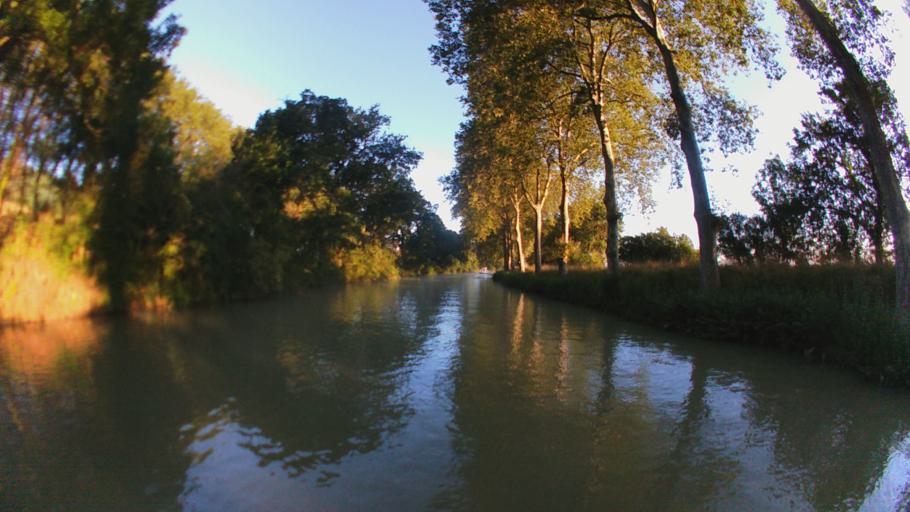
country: FR
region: Midi-Pyrenees
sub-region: Departement de la Haute-Garonne
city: Gardouch
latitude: 43.4039
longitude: 1.6681
